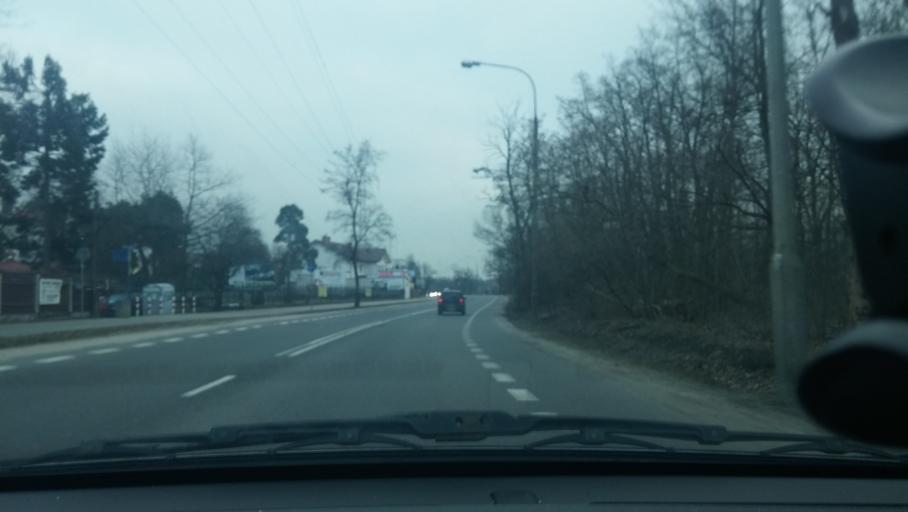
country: PL
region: Masovian Voivodeship
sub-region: Warszawa
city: Wawer
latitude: 52.2190
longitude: 21.1550
